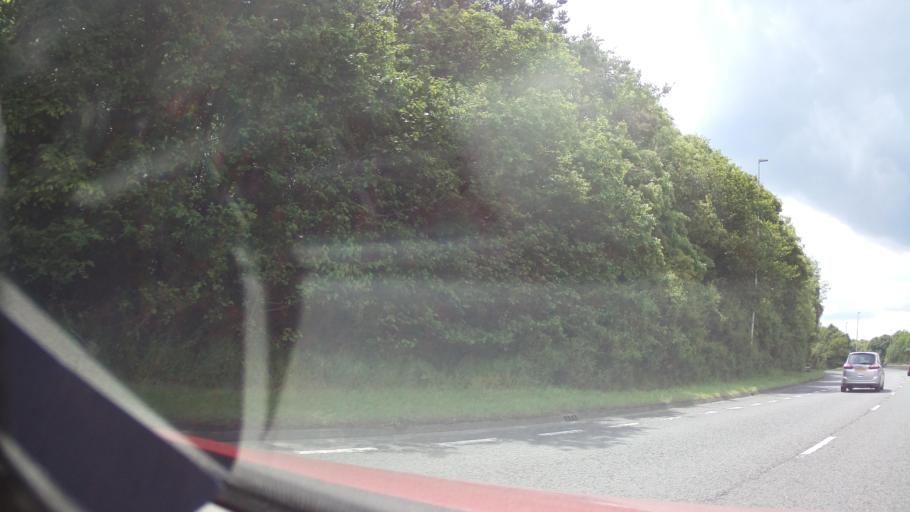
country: GB
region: England
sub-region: Sunderland
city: Washington
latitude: 54.9061
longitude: -1.5236
